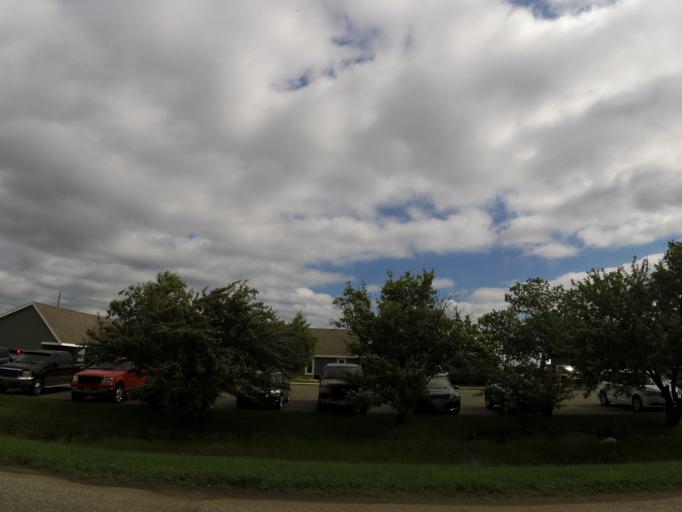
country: US
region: Minnesota
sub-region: Polk County
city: East Grand Forks
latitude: 47.9186
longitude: -96.9903
